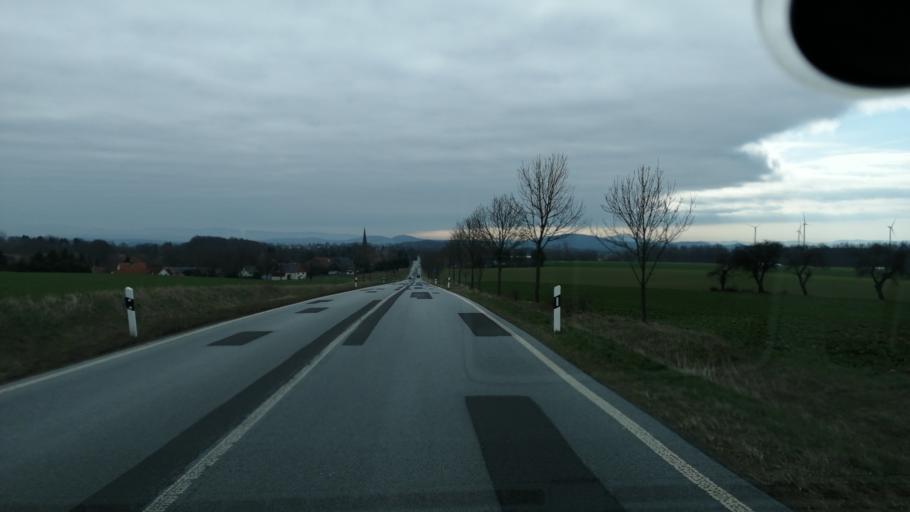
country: DE
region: Saxony
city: Herrnhut
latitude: 51.0355
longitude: 14.7132
